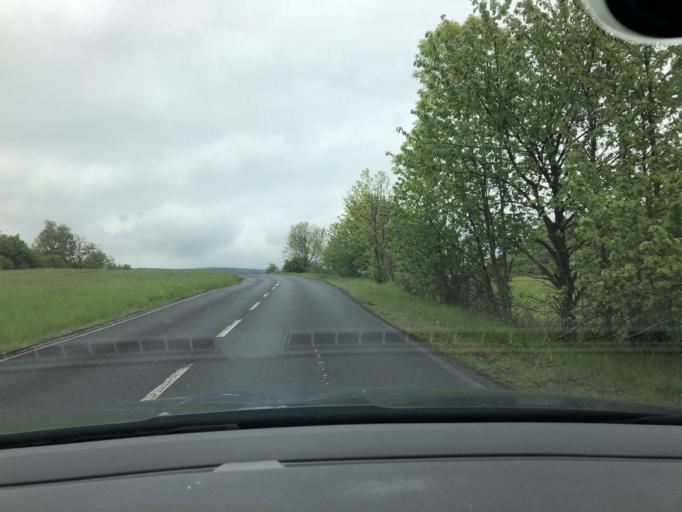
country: CZ
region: Ustecky
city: Libouchec
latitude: 50.7136
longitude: 14.0111
